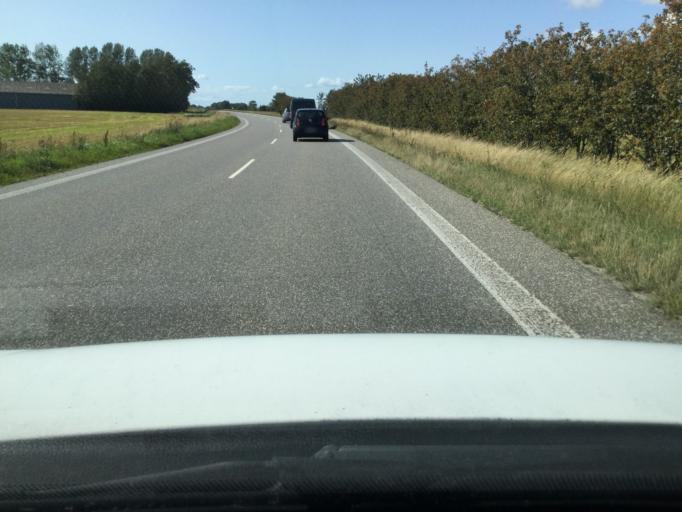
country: DK
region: Zealand
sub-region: Lolland Kommune
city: Nakskov
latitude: 54.8088
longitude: 11.2210
